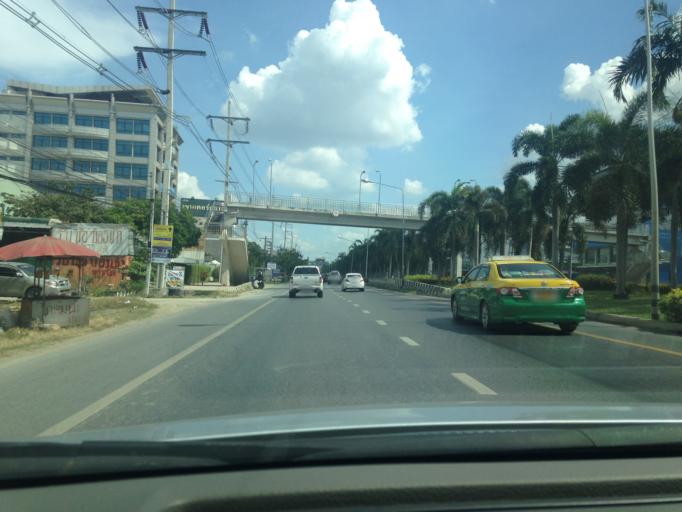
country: TH
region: Phra Nakhon Si Ayutthaya
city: Ban Bang Kadi Pathum Thani
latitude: 13.9889
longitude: 100.5843
